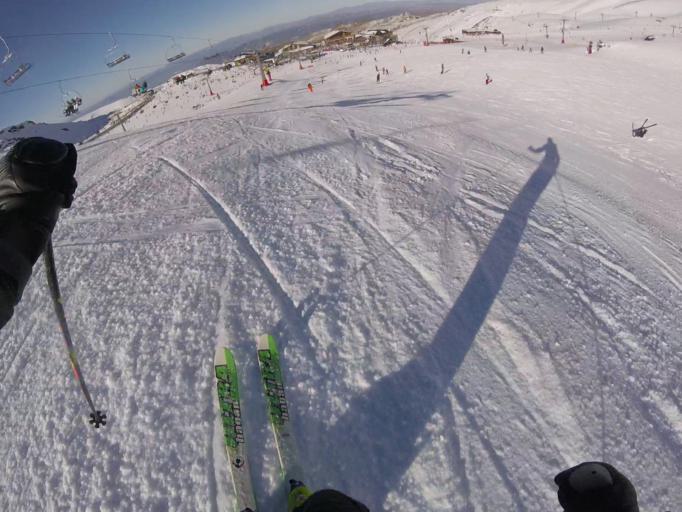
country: ES
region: Andalusia
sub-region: Provincia de Granada
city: Guejar-Sierra
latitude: 37.0684
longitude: -3.3876
